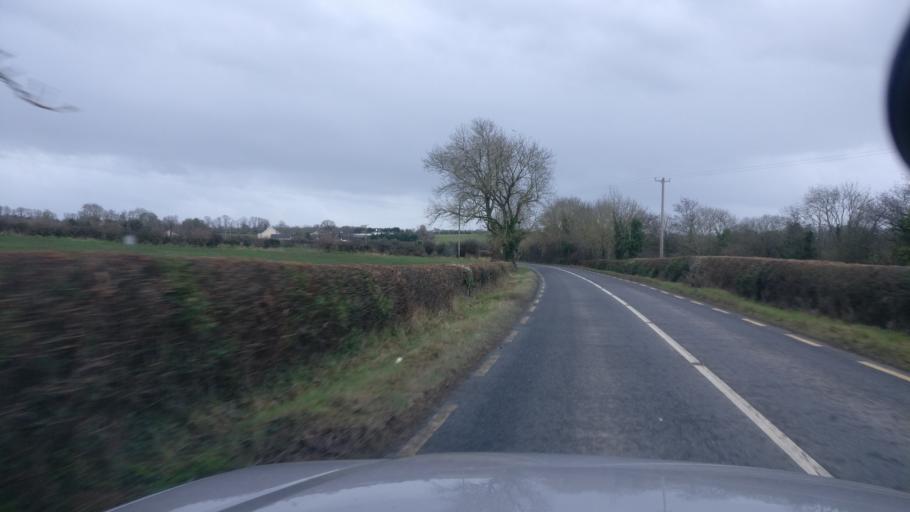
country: IE
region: Leinster
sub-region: Kilkenny
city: Thomastown
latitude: 52.5547
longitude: -7.2275
